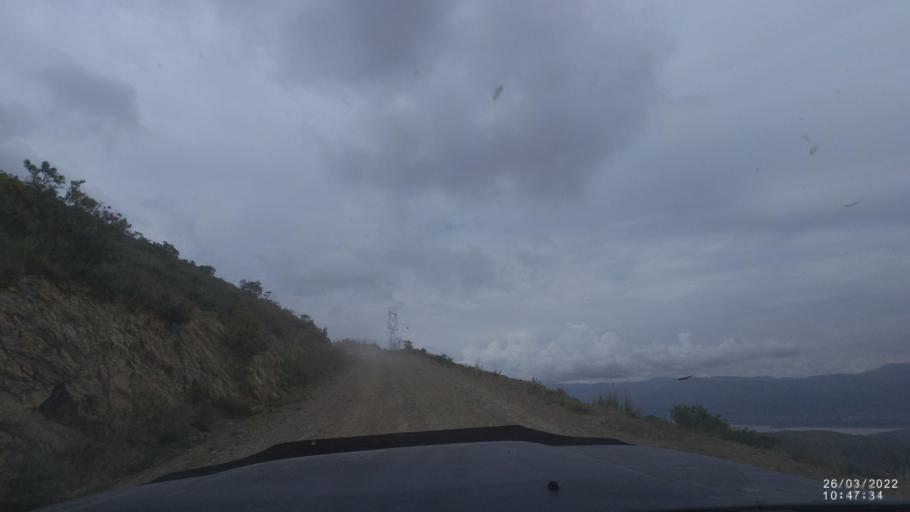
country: BO
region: Cochabamba
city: Tarata
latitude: -17.4927
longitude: -66.0491
